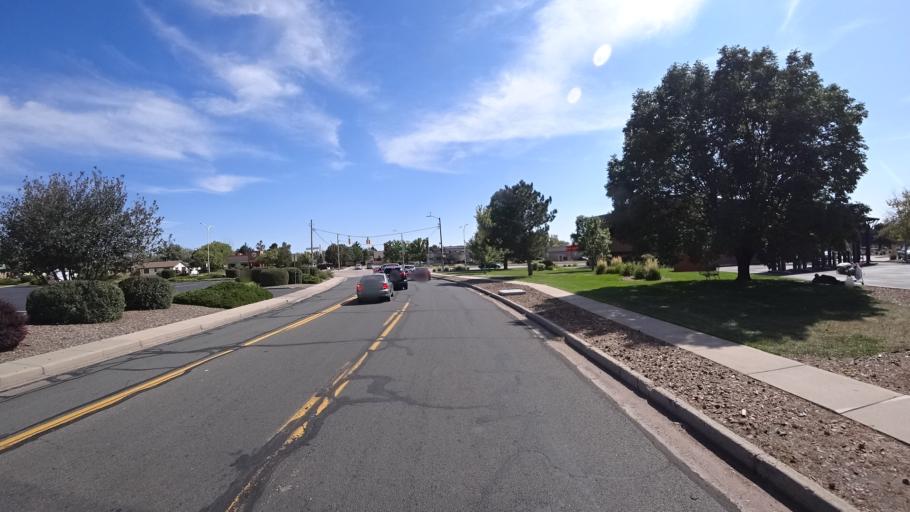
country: US
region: Colorado
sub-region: El Paso County
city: Cimarron Hills
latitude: 38.8933
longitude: -104.7534
